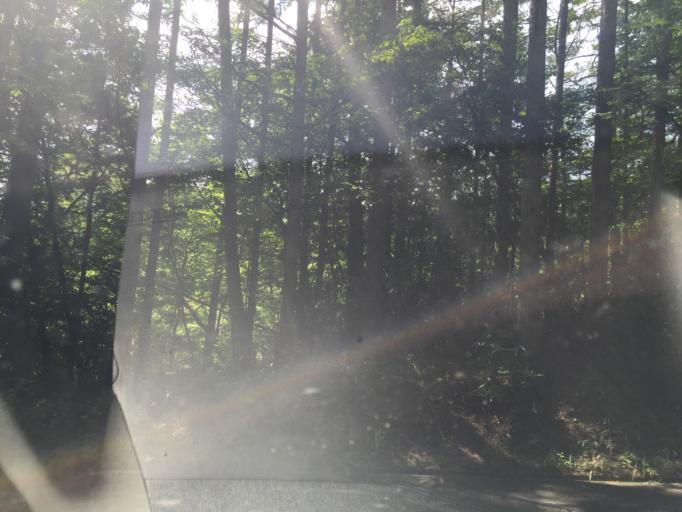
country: JP
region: Nagano
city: Iida
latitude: 35.3773
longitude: 137.6936
